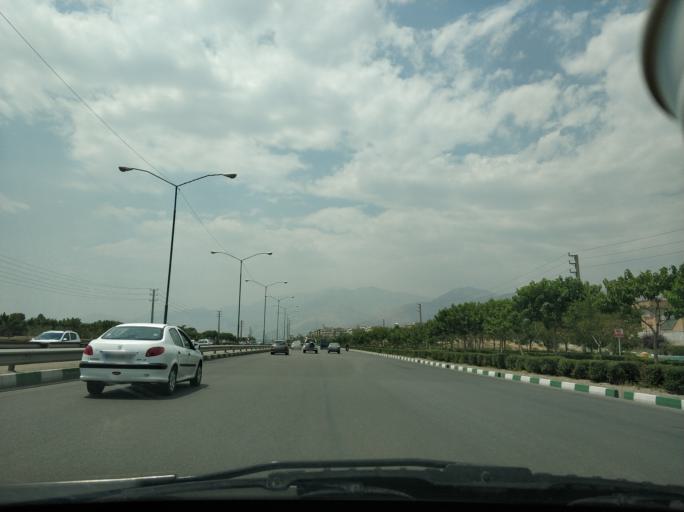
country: IR
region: Tehran
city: Tajrish
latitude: 35.7624
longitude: 51.5692
